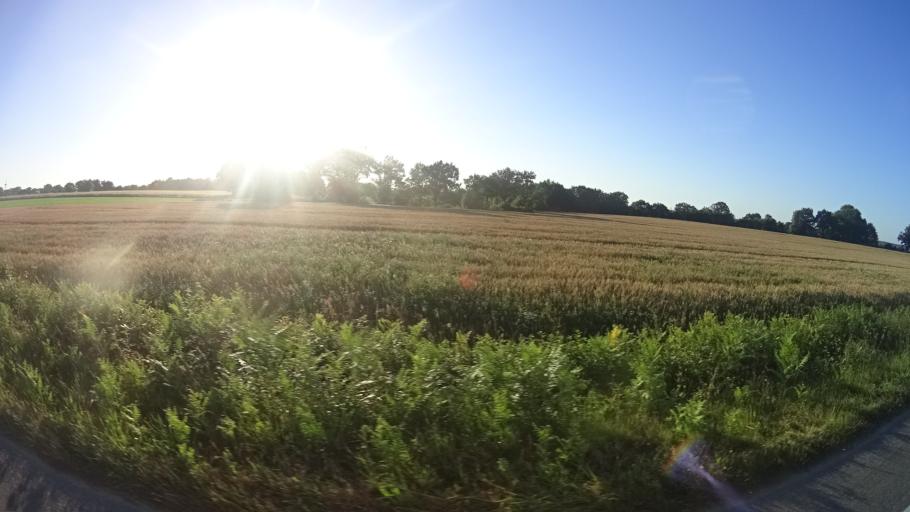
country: FR
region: Brittany
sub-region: Departement d'Ille-et-Vilaine
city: La Dominelais
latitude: 47.7510
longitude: -1.7034
